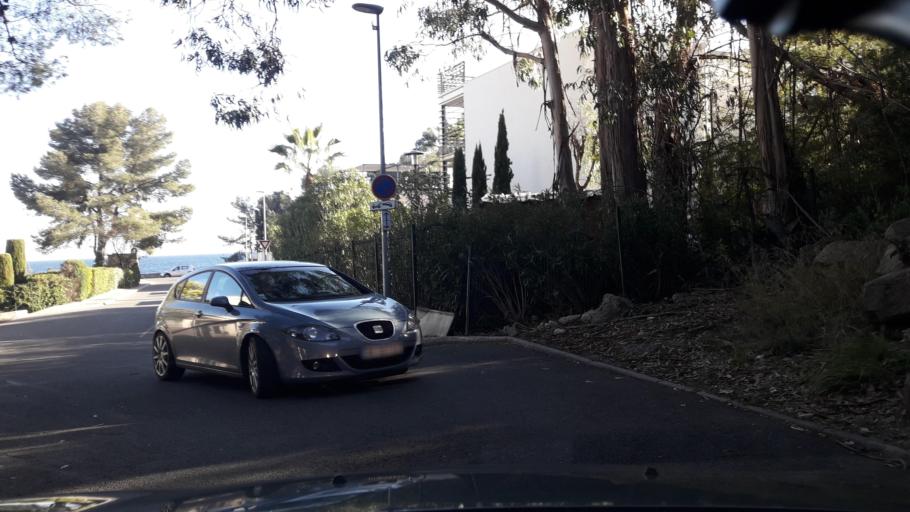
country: FR
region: Provence-Alpes-Cote d'Azur
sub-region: Departement du Var
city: Saint-Raphael
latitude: 43.4185
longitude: 6.8217
